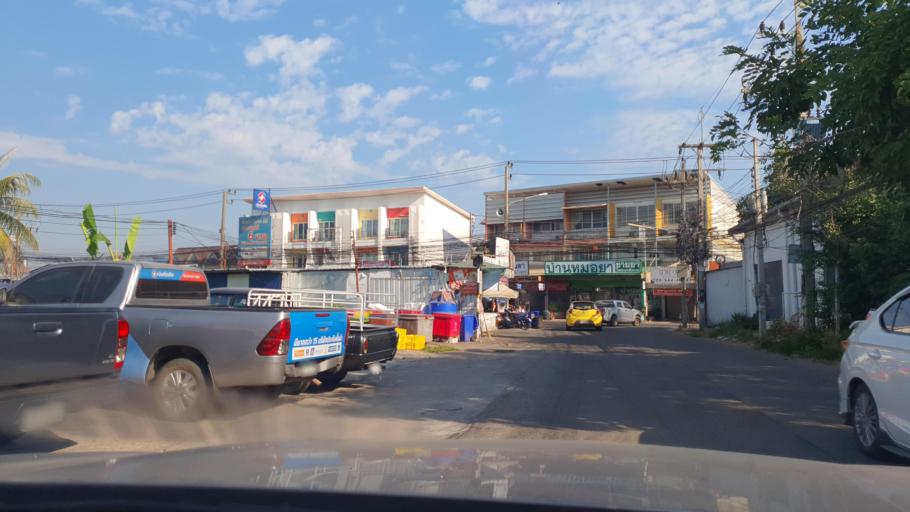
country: TH
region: Khon Kaen
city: Khon Kaen
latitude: 16.4211
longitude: 102.8062
